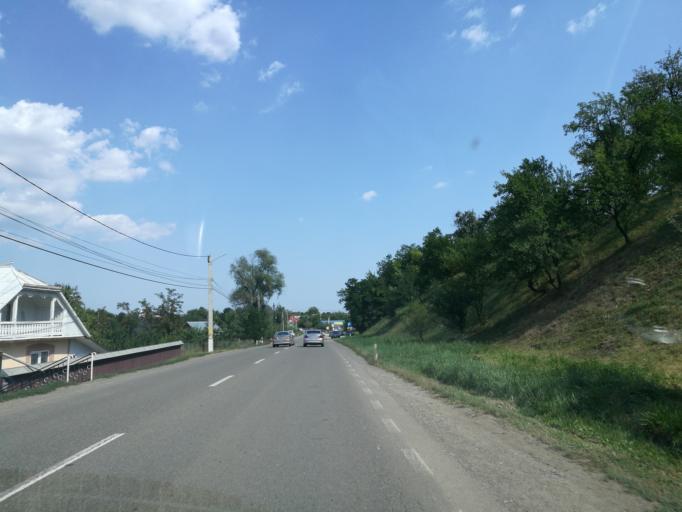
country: RO
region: Neamt
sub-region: Comuna Baltatesti
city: Valea Seaca
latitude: 47.1285
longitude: 26.3143
